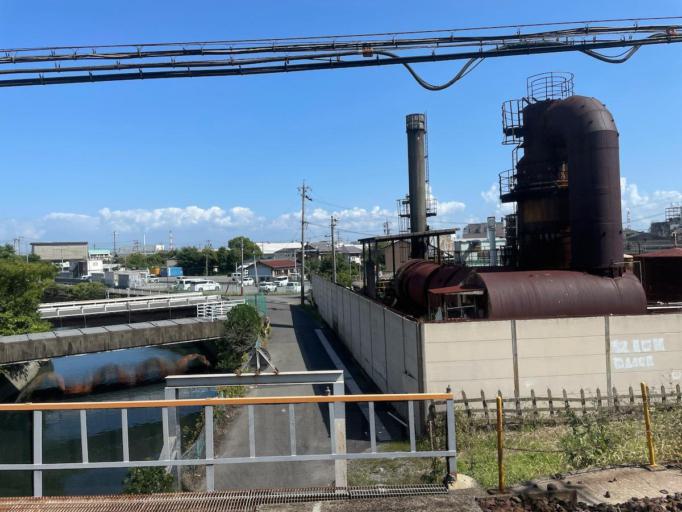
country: JP
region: Mie
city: Yokkaichi
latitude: 34.9480
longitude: 136.6220
